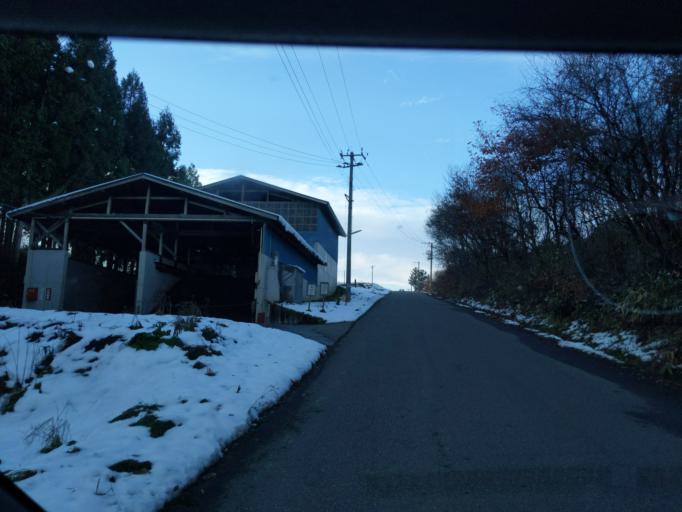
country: JP
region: Iwate
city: Mizusawa
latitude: 39.0438
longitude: 141.1124
